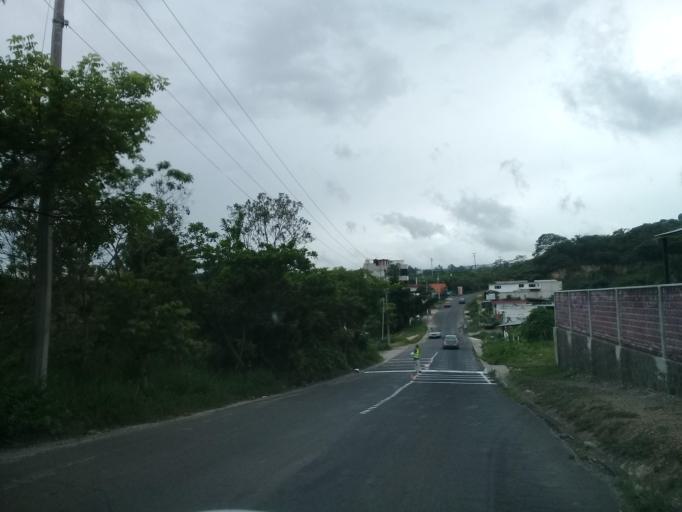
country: MX
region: Veracruz
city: El Castillo
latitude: 19.5553
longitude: -96.8536
